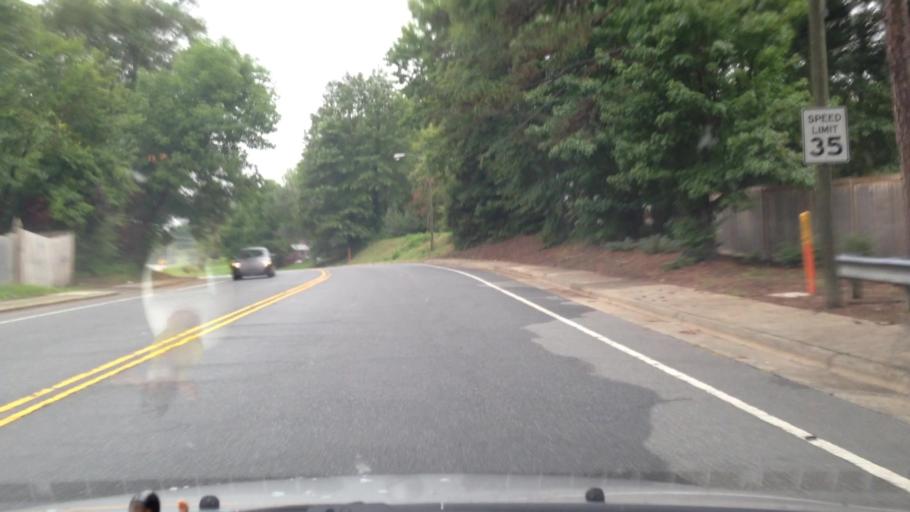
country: US
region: North Carolina
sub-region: Guilford County
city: Greensboro
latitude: 36.0547
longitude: -79.7693
